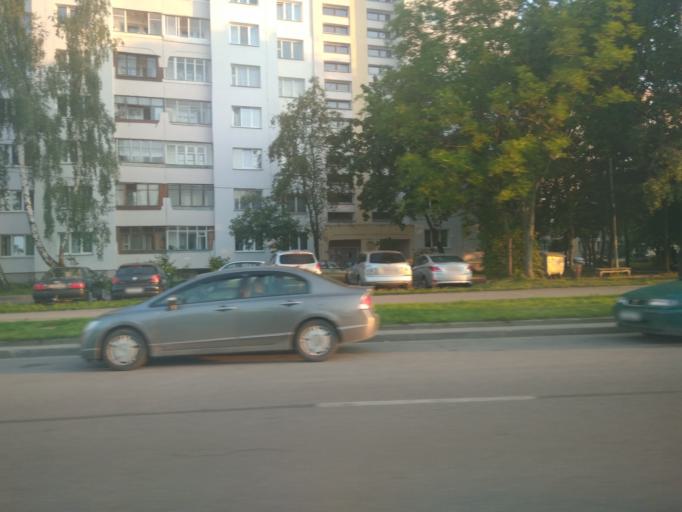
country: BY
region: Minsk
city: Novoye Medvezhino
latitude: 53.9286
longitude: 27.4838
